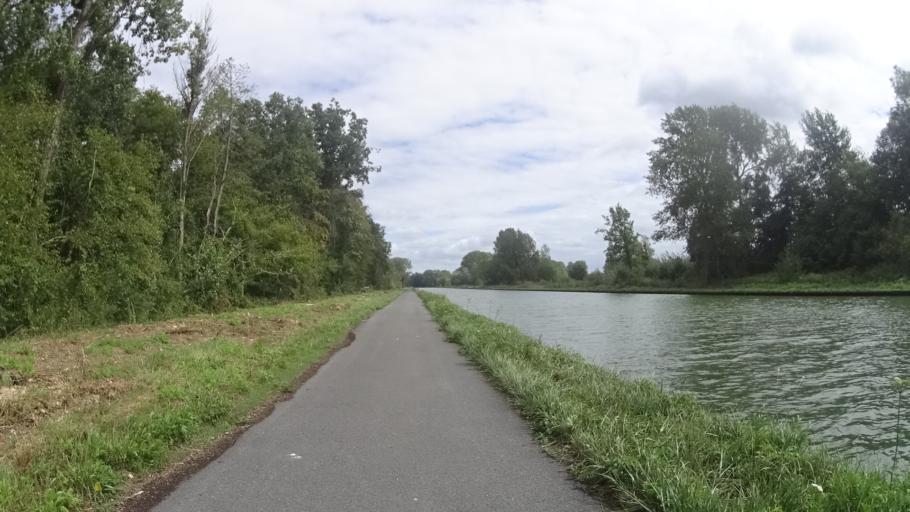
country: FR
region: Picardie
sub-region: Departement de l'Aisne
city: Ognes
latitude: 49.5803
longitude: 3.1503
